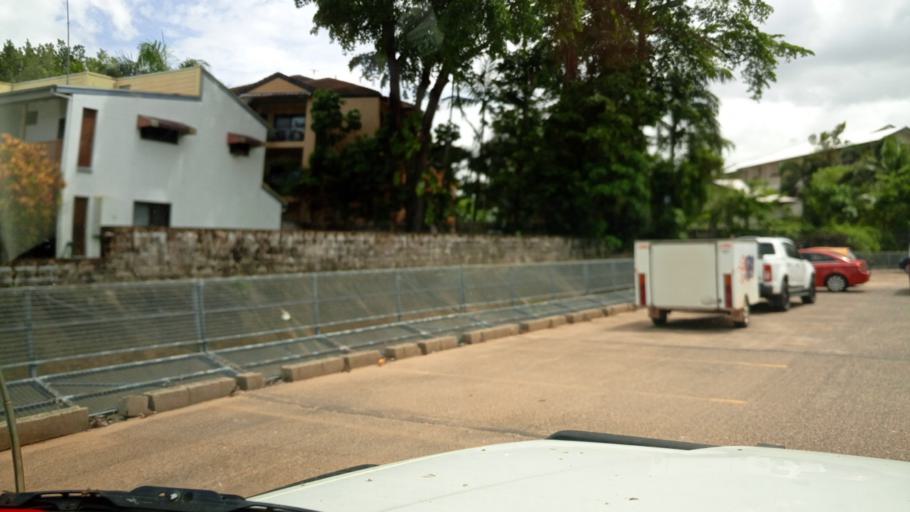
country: AU
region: Queensland
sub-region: Cairns
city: Woree
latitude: -16.9446
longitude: 145.7413
